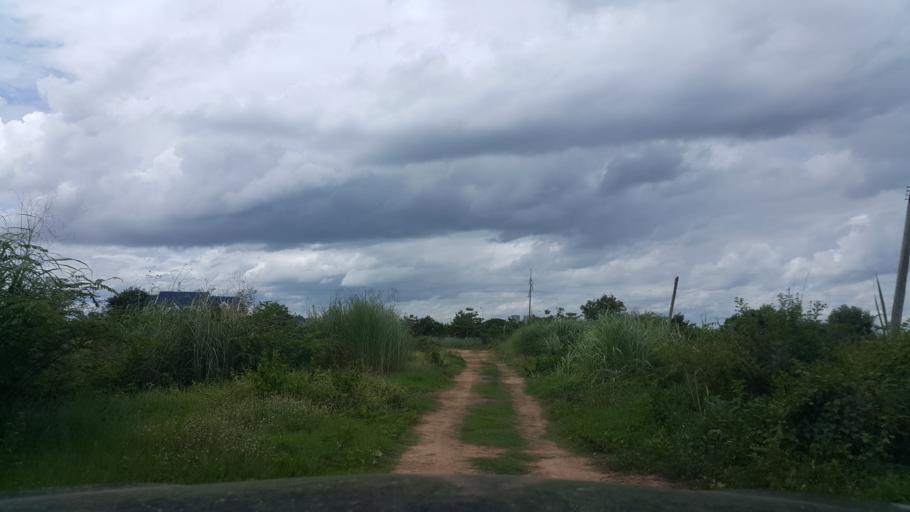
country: TH
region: Sukhothai
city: Sukhothai
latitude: 17.0320
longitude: 99.7994
